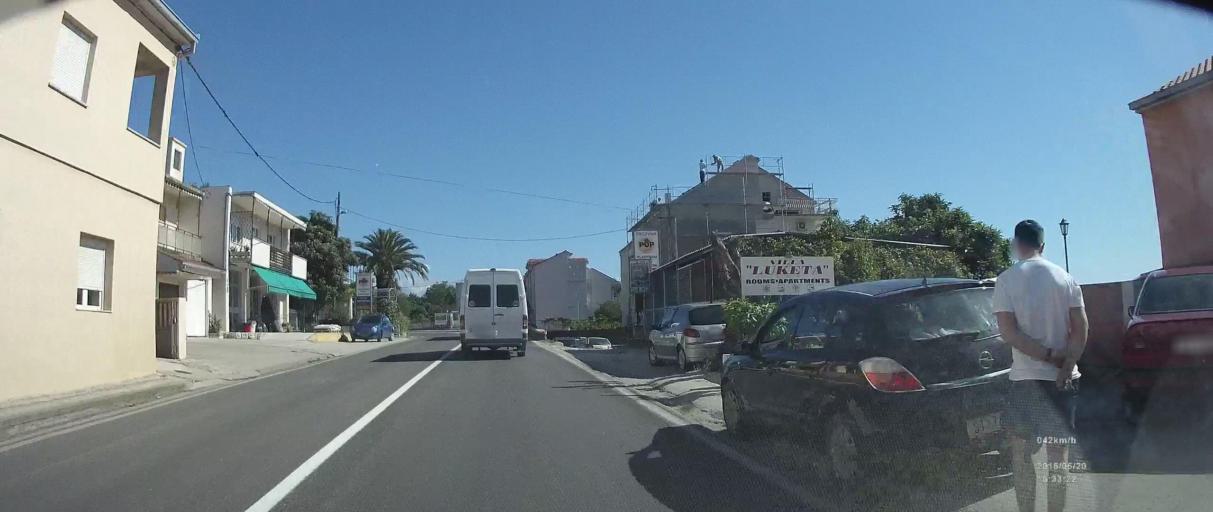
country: HR
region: Splitsko-Dalmatinska
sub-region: Grad Split
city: Stobrec
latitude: 43.4969
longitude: 16.5371
